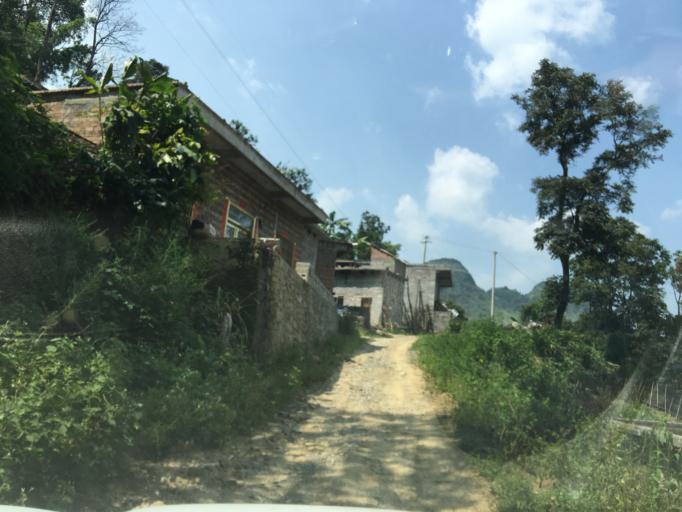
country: CN
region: Guangxi Zhuangzu Zizhiqu
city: Xinzhou
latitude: 24.9897
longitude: 105.7401
